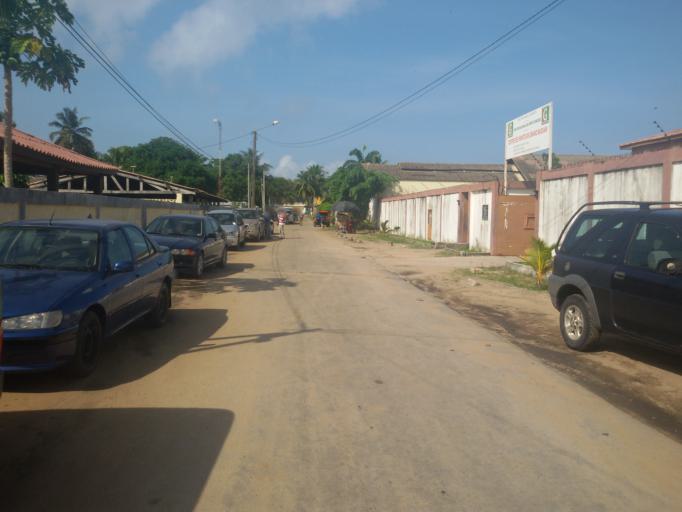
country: CI
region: Sud-Comoe
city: Grand-Bassam
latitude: 5.1967
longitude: -3.7346
